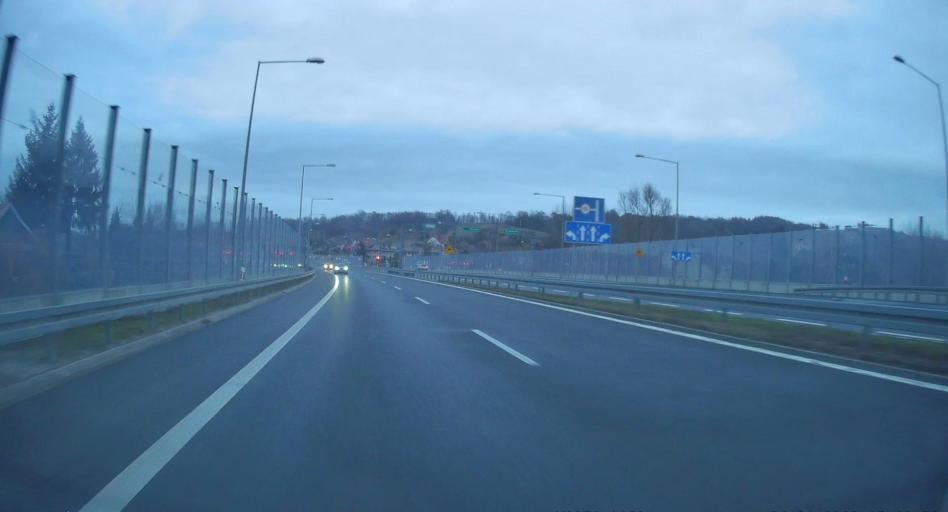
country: PL
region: Subcarpathian Voivodeship
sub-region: Powiat ropczycko-sedziszowski
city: Ropczyce
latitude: 50.0507
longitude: 21.6026
